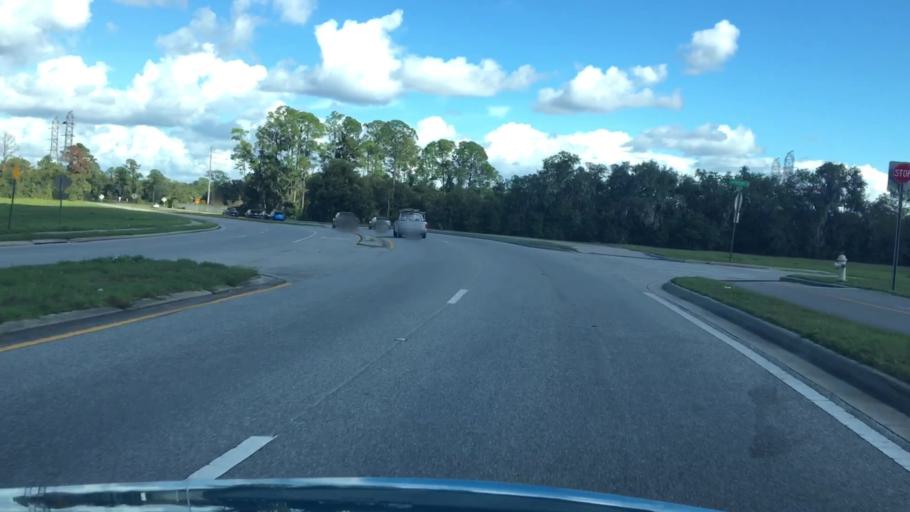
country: US
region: Florida
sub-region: Volusia County
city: Deltona
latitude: 28.8719
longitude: -81.2766
